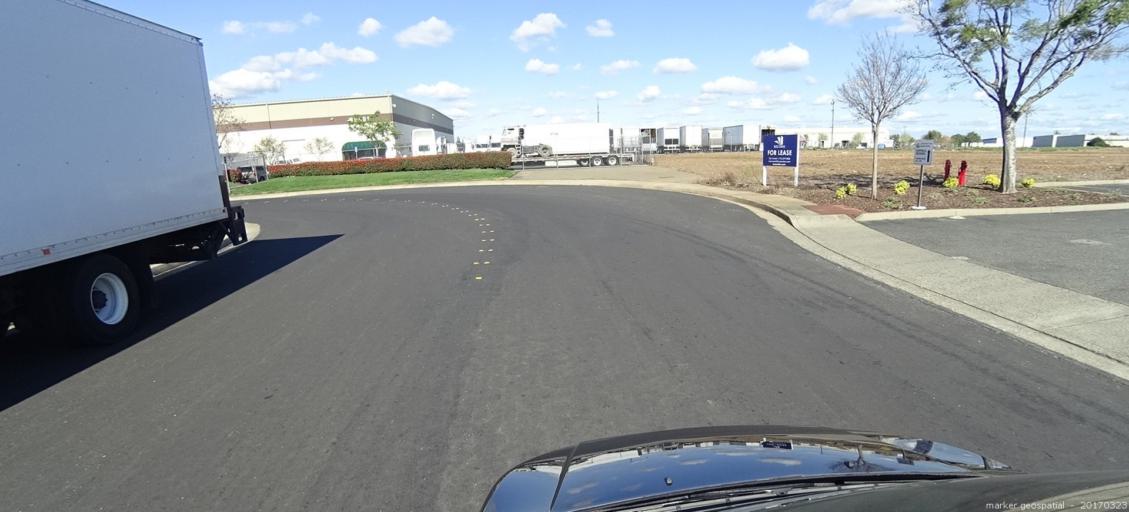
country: US
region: California
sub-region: Sacramento County
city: Florin
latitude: 38.5151
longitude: -121.3784
